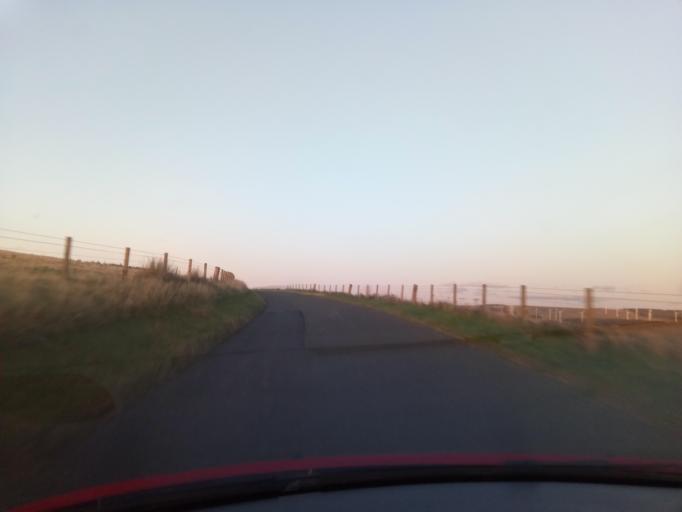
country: GB
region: Scotland
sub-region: East Lothian
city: Pencaitland
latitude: 55.8102
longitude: -2.8787
